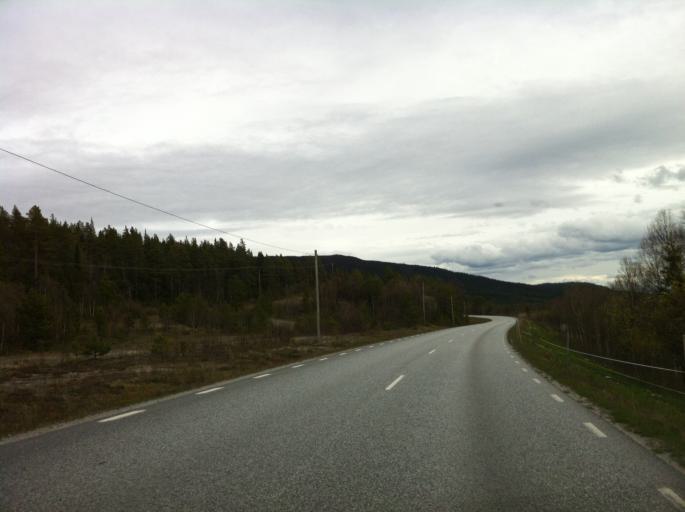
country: NO
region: Sor-Trondelag
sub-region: Tydal
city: Aas
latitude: 62.6159
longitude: 12.4875
